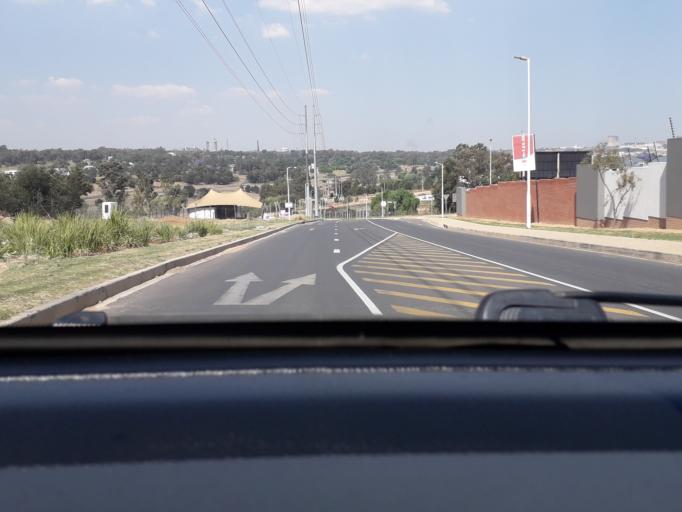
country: ZA
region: Gauteng
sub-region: City of Johannesburg Metropolitan Municipality
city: Modderfontein
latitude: -26.0944
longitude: 28.1409
